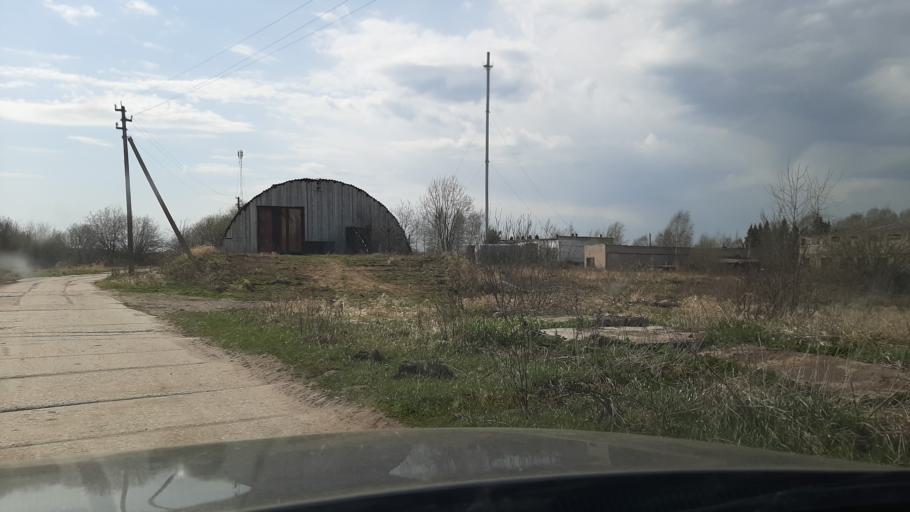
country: RU
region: Ivanovo
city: Privolzhsk
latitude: 57.3282
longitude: 41.2354
